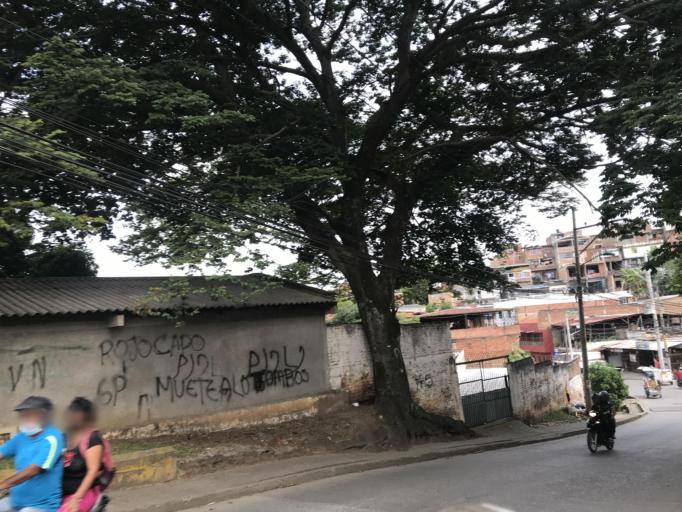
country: CO
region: Valle del Cauca
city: Cali
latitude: 3.3752
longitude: -76.5506
